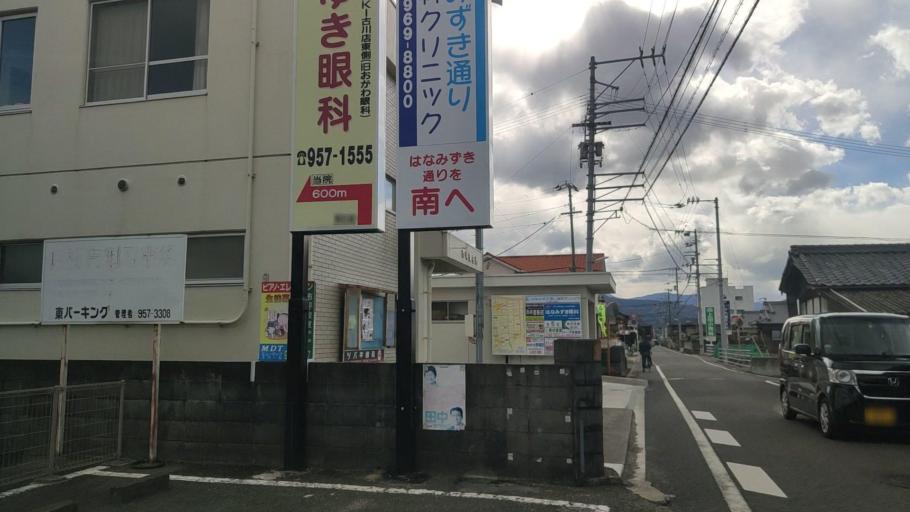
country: JP
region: Ehime
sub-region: Shikoku-chuo Shi
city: Matsuyama
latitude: 33.8119
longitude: 132.7525
